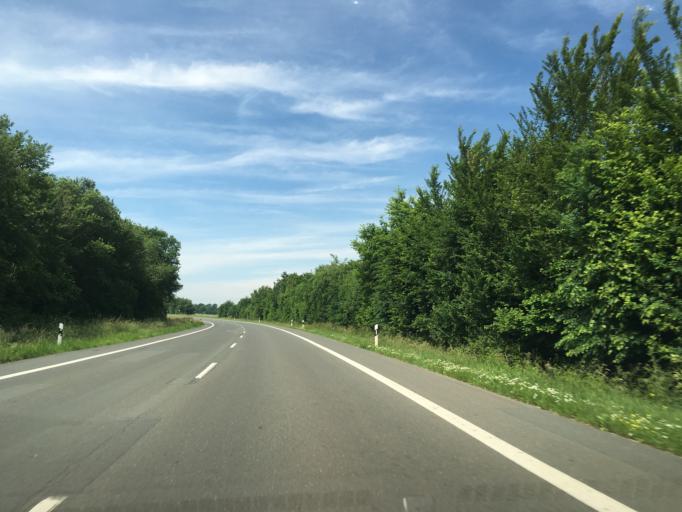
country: DE
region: North Rhine-Westphalia
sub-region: Regierungsbezirk Munster
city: Steinfurt
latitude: 52.1485
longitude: 7.3984
